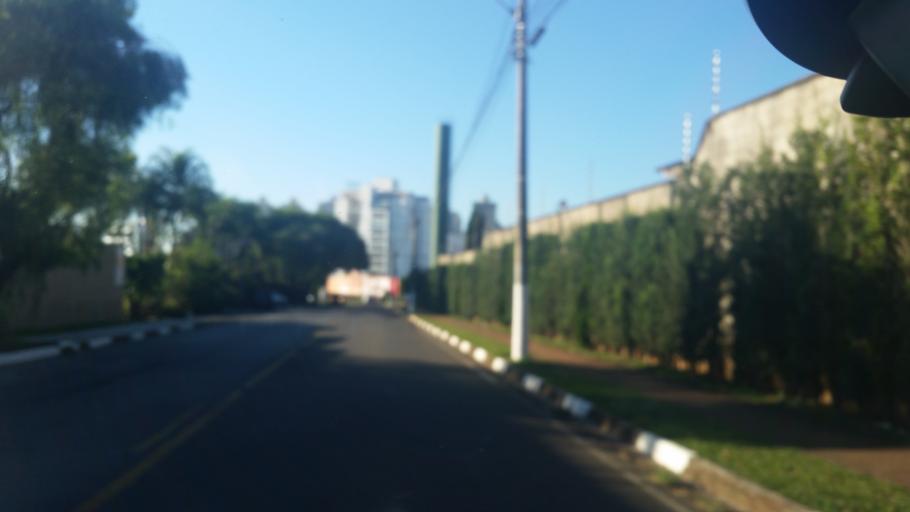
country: BR
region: Sao Paulo
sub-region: Campinas
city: Campinas
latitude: -22.8610
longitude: -47.0538
